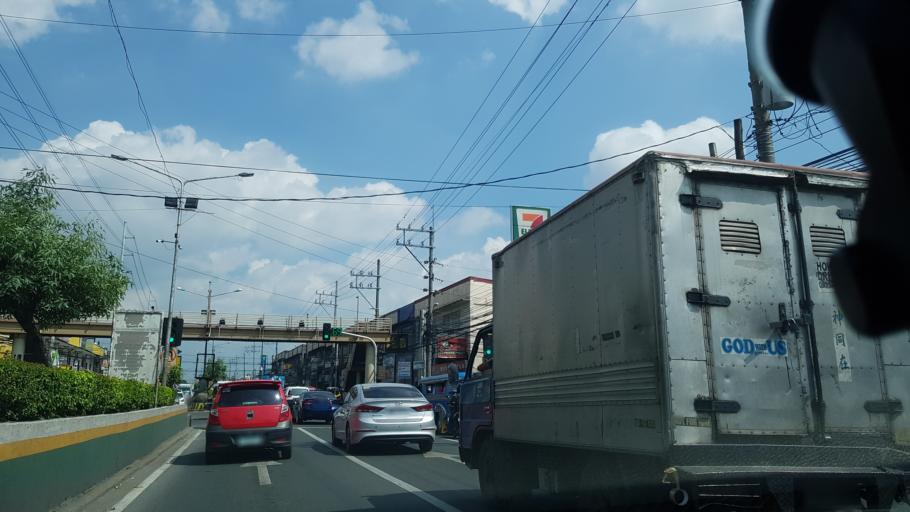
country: PH
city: Sambayanihan People's Village
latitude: 14.4688
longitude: 121.0115
